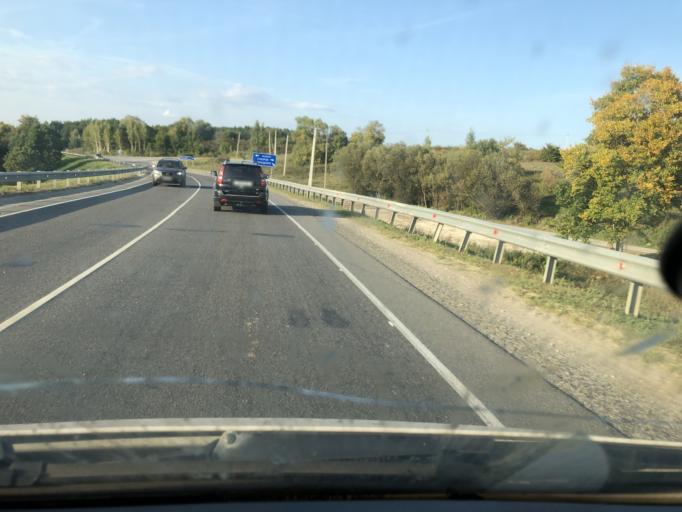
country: RU
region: Kaluga
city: Peremyshl'
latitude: 54.2957
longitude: 36.1795
